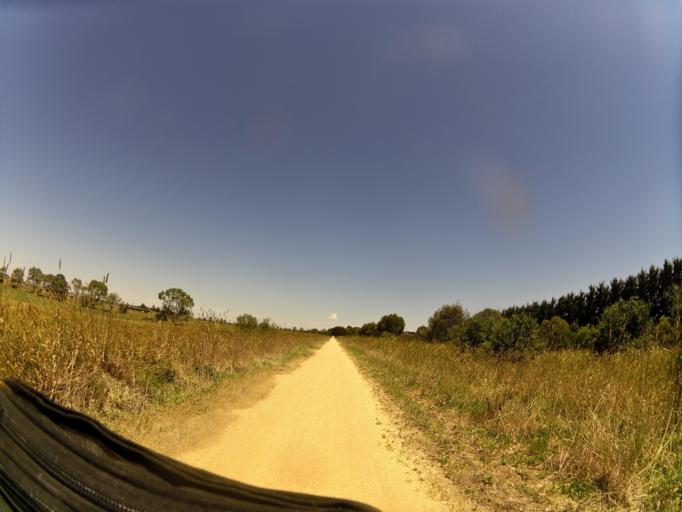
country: AU
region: Victoria
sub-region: Wellington
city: Sale
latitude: -37.9801
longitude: 147.0534
